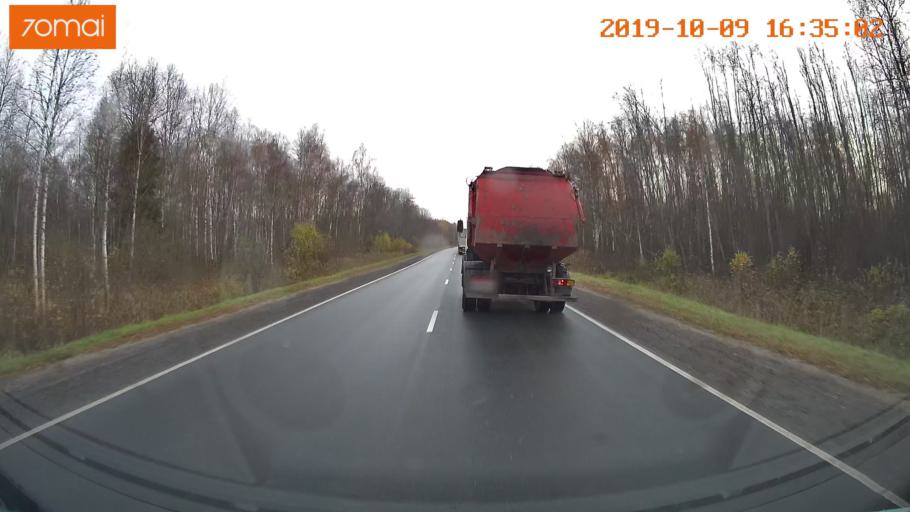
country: RU
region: Kostroma
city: Oktyabr'skiy
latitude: 57.5598
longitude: 40.9970
